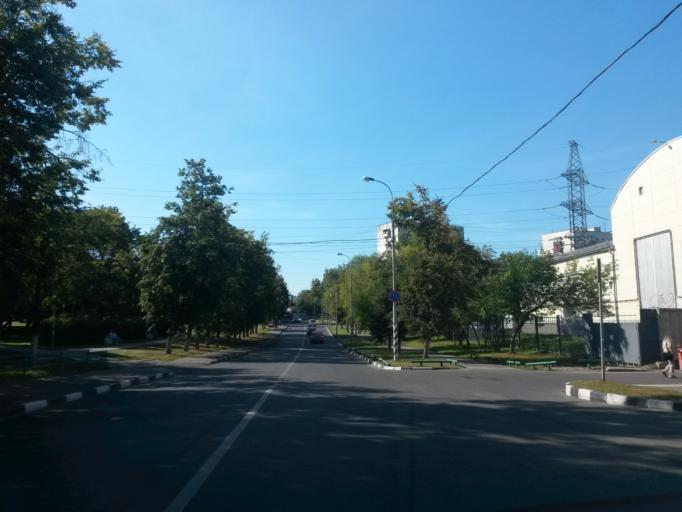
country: RU
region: Moscow
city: Kotlovka
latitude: 55.6598
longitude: 37.5907
